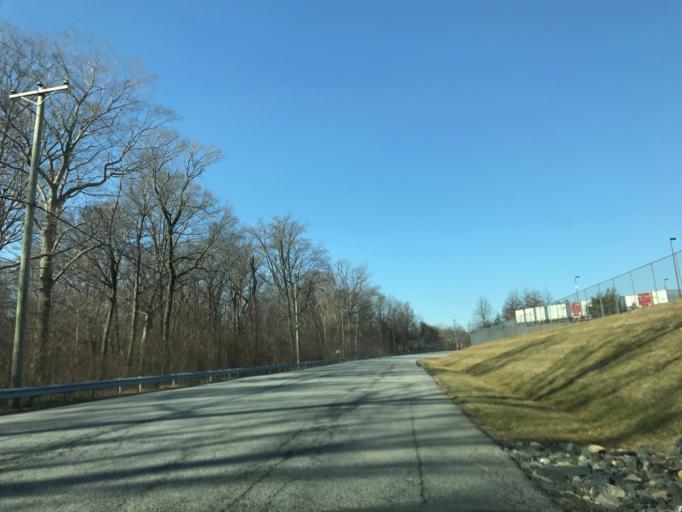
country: US
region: Maryland
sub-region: Cecil County
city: Perryville
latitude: 39.5575
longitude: -76.0601
